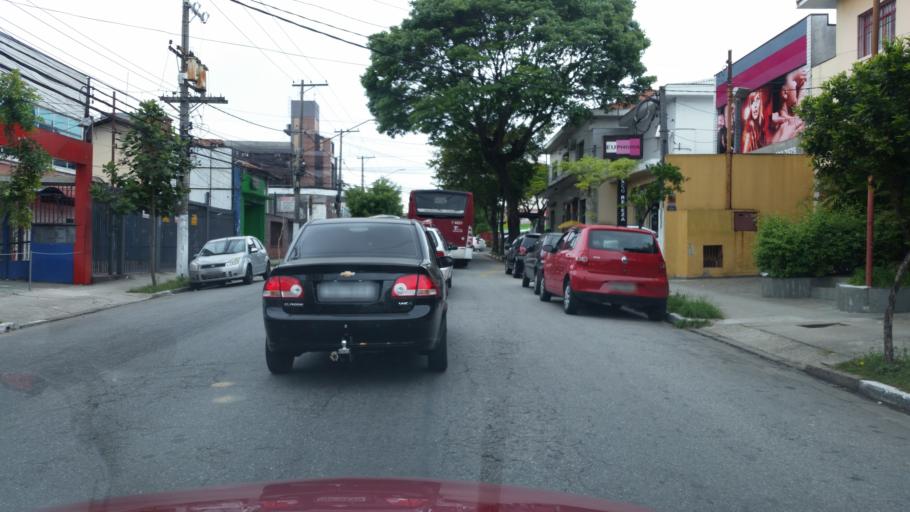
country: BR
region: Sao Paulo
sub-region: Diadema
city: Diadema
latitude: -23.6400
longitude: -46.6686
